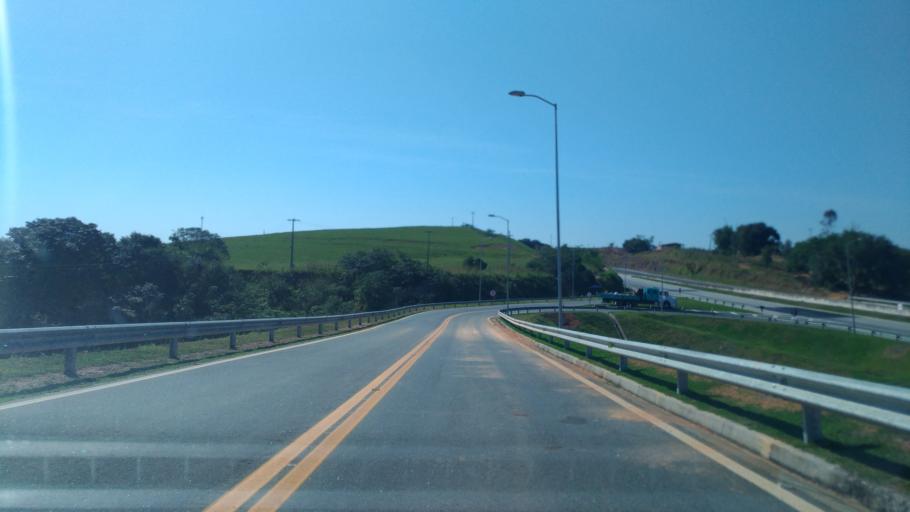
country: BR
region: Rio de Janeiro
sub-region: Sao Fidelis
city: Sao Fidelis
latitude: -21.9797
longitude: -41.6581
